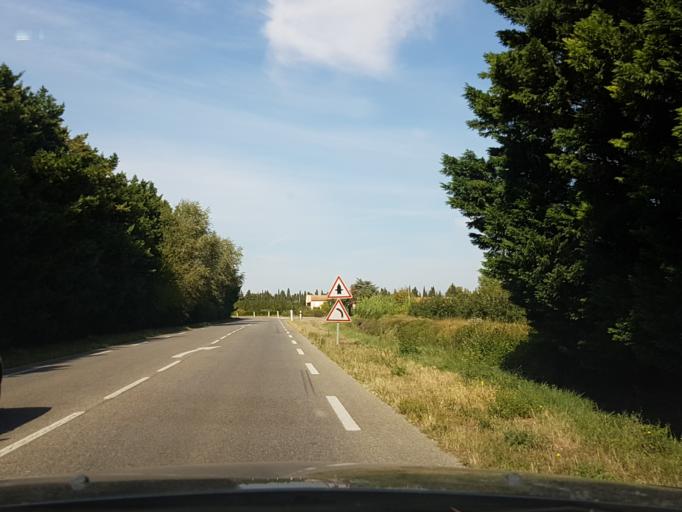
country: FR
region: Provence-Alpes-Cote d'Azur
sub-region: Departement des Bouches-du-Rhone
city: Noves
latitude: 43.8601
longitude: 4.9025
